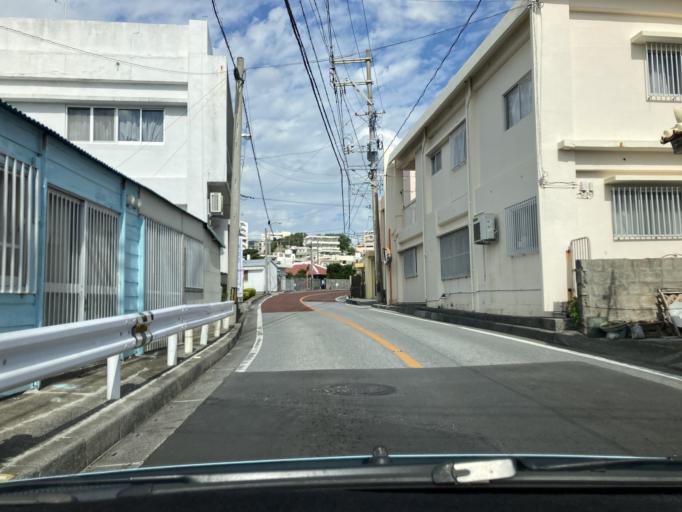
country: JP
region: Okinawa
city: Chatan
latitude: 26.3139
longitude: 127.7708
